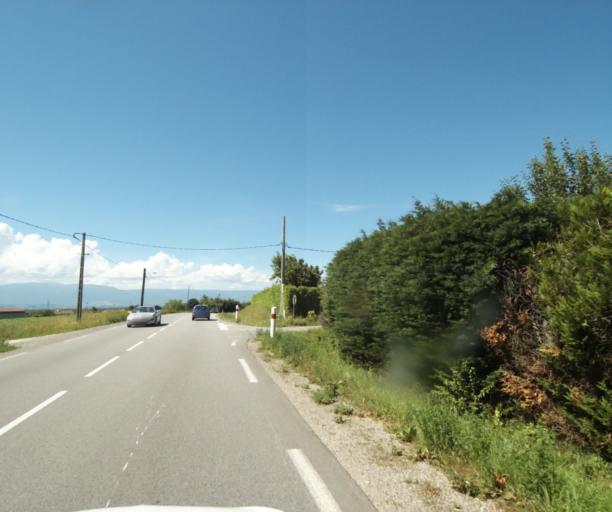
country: FR
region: Rhone-Alpes
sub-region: Departement de la Haute-Savoie
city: Loisin
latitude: 46.2815
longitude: 6.3101
